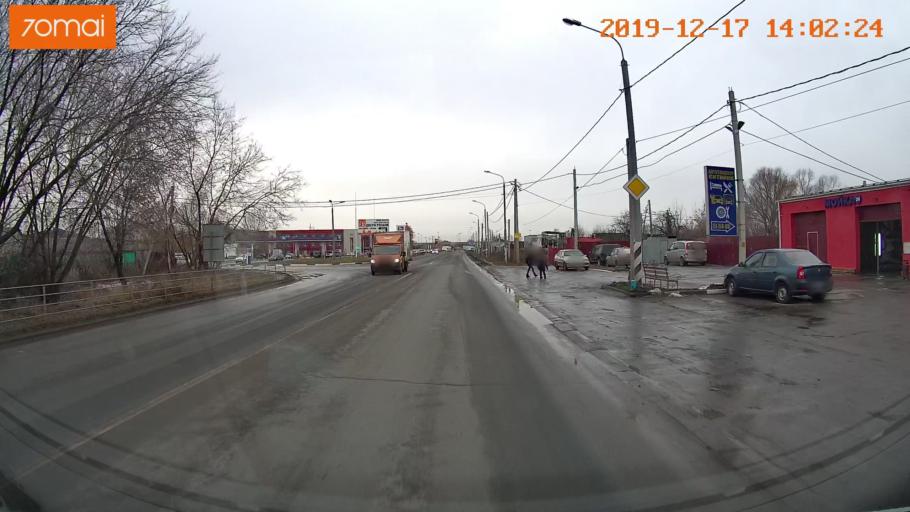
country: RU
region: Rjazan
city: Ryazan'
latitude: 54.6147
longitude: 39.6481
